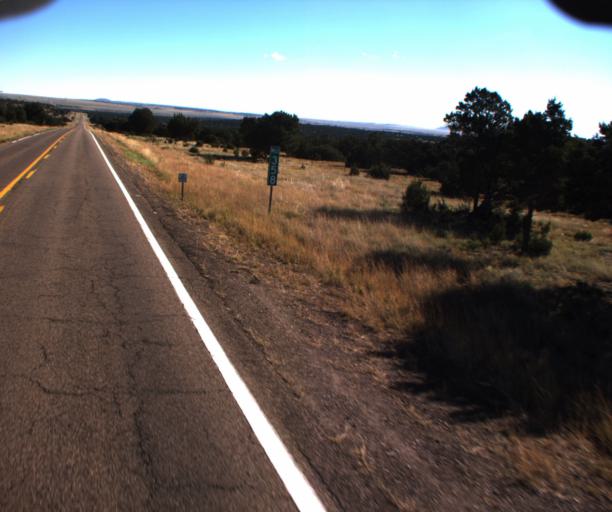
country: US
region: Arizona
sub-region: Navajo County
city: White Mountain Lake
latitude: 34.3204
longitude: -109.7610
